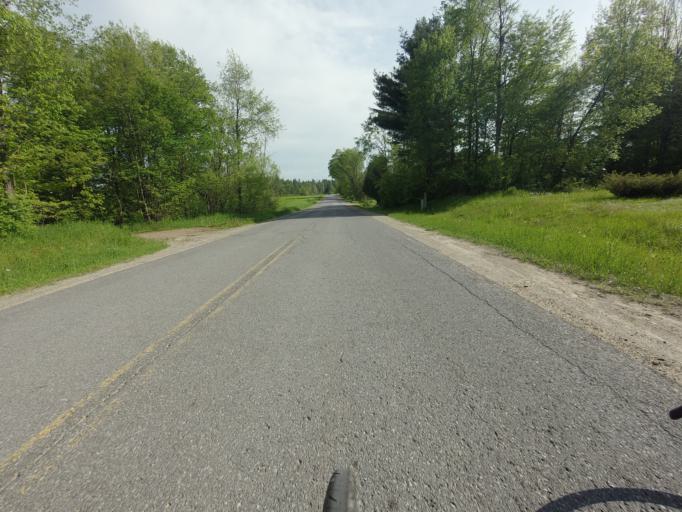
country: US
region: New York
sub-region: St. Lawrence County
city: Gouverneur
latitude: 44.2498
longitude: -75.2215
